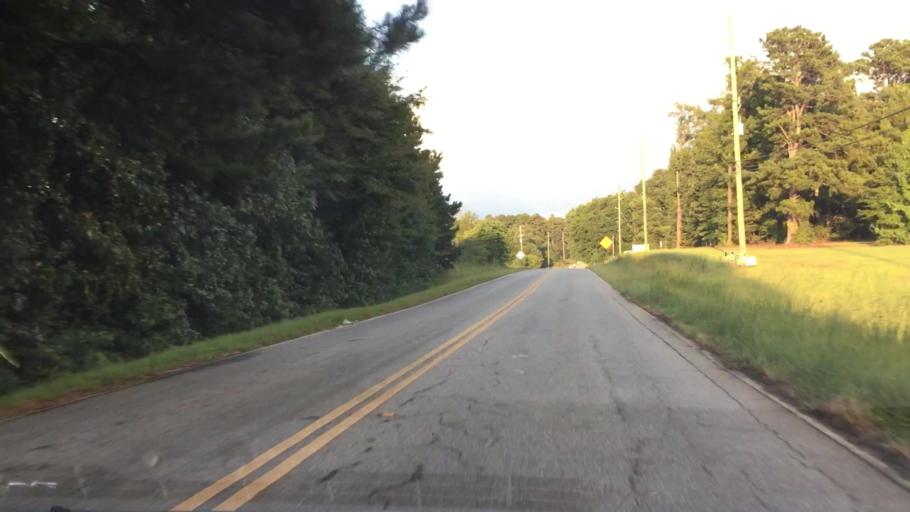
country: US
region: Georgia
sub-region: Henry County
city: McDonough
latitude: 33.4914
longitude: -84.1752
